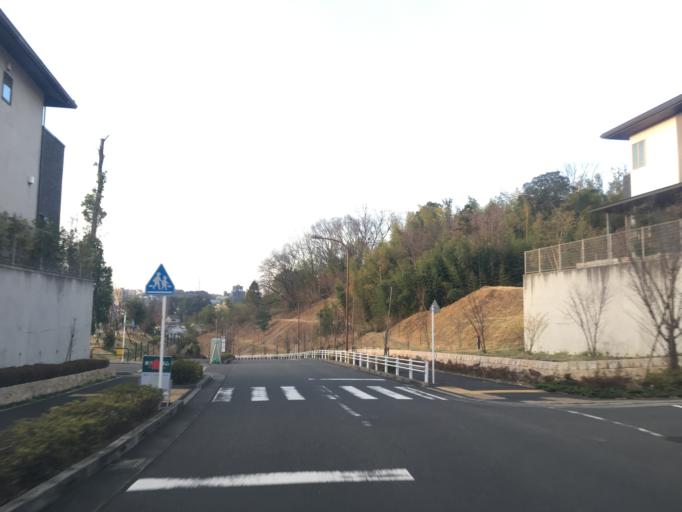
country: JP
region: Tokyo
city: Hino
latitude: 35.6346
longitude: 139.3981
